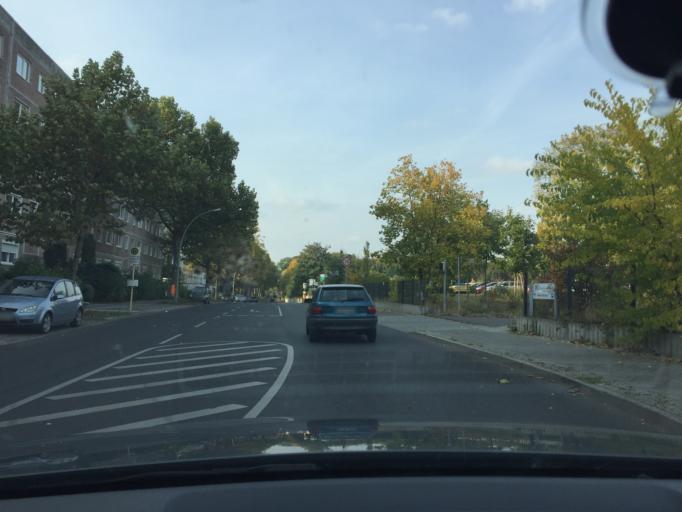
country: DE
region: Berlin
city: Buch
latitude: 52.6298
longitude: 13.5051
